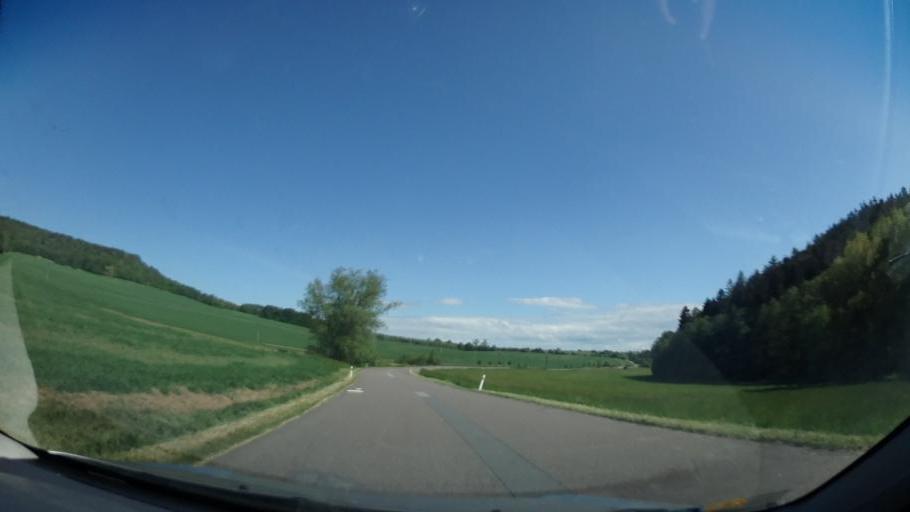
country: CZ
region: South Moravian
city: Velke Opatovice
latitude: 49.6411
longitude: 16.6144
